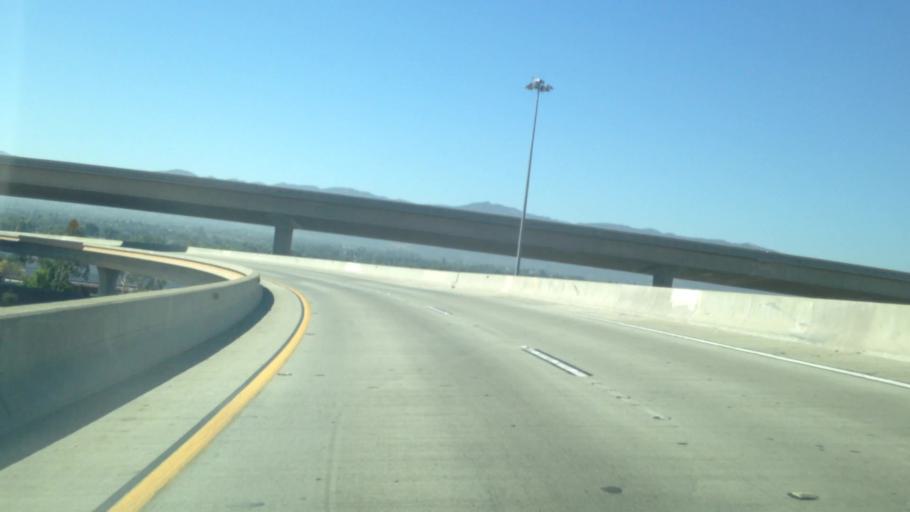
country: US
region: California
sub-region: Riverside County
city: Home Gardens
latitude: 33.8821
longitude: -117.5411
